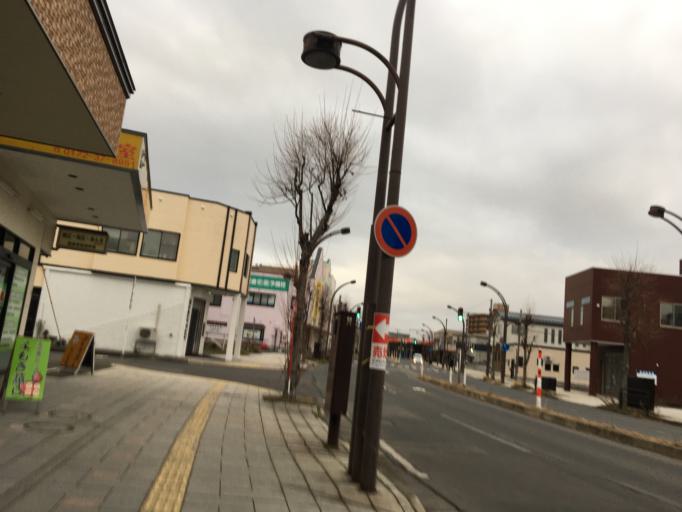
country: JP
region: Aomori
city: Hirosaki
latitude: 40.5958
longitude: 140.4806
